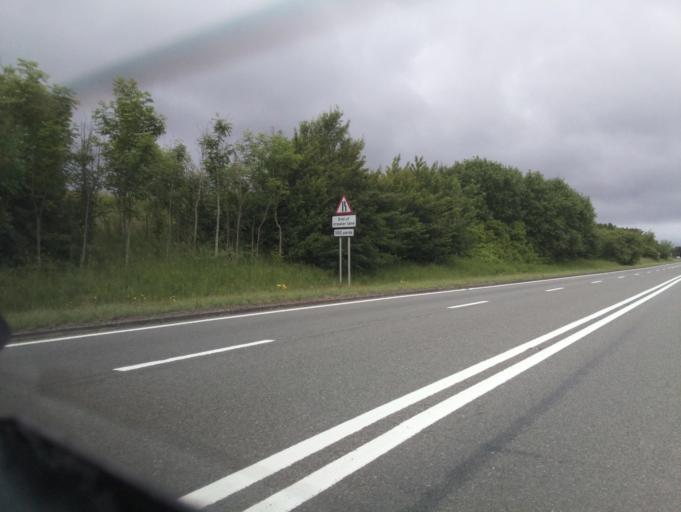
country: GB
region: England
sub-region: Leicestershire
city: Ashby de la Zouch
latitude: 52.7657
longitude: -1.4970
